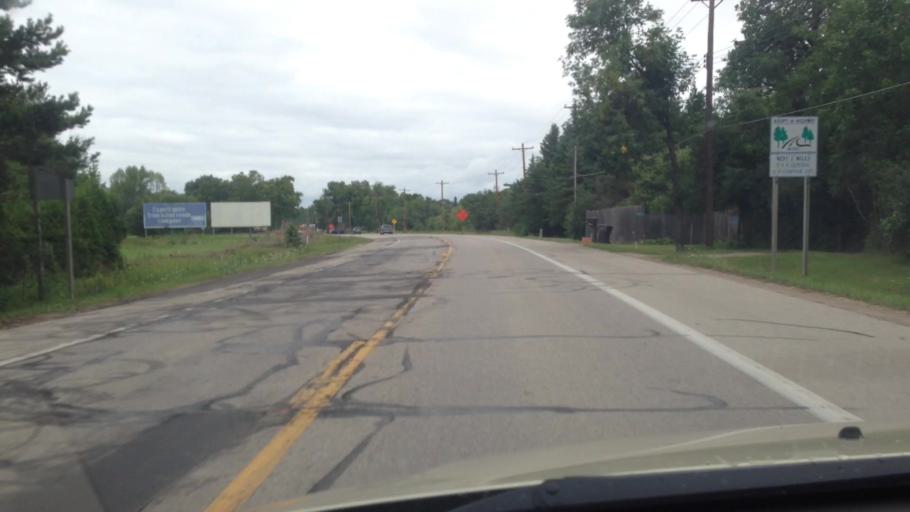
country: US
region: Michigan
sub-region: Delta County
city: Escanaba
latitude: 45.6931
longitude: -87.1006
